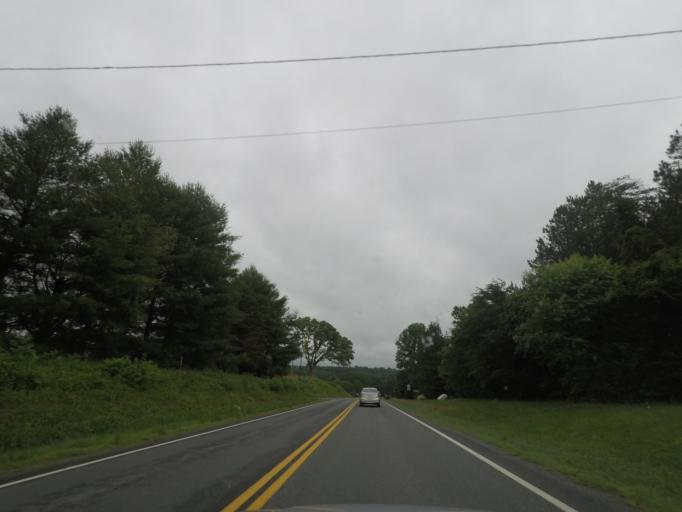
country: US
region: Virginia
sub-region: Fluvanna County
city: Palmyra
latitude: 37.8485
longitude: -78.2718
